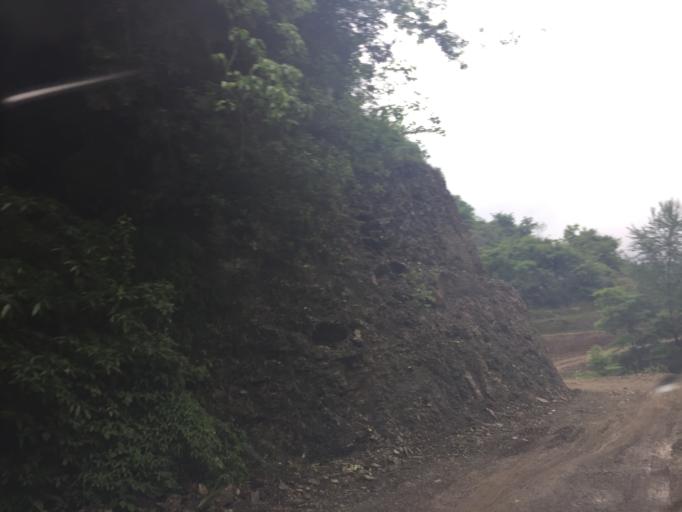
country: CN
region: Guizhou Sheng
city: Kuanping
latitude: 28.0057
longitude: 108.0403
